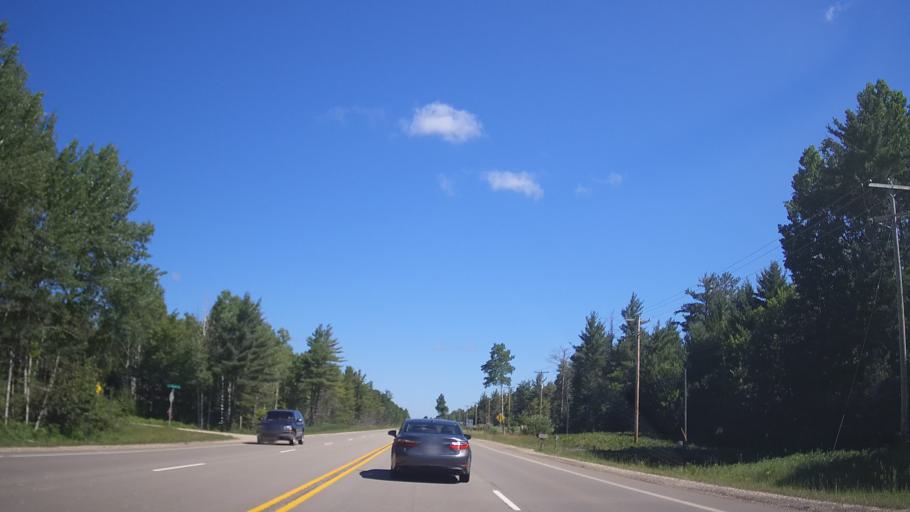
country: US
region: Michigan
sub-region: Cheboygan County
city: Indian River
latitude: 45.5213
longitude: -84.7817
